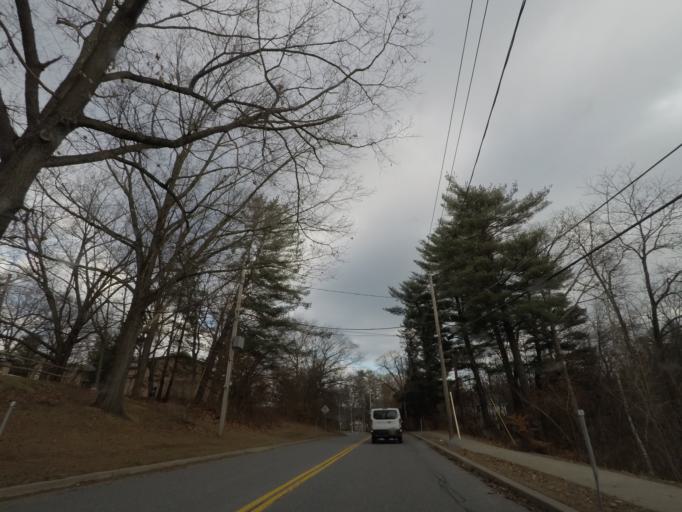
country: US
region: New York
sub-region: Albany County
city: Westmere
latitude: 42.6847
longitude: -73.8697
